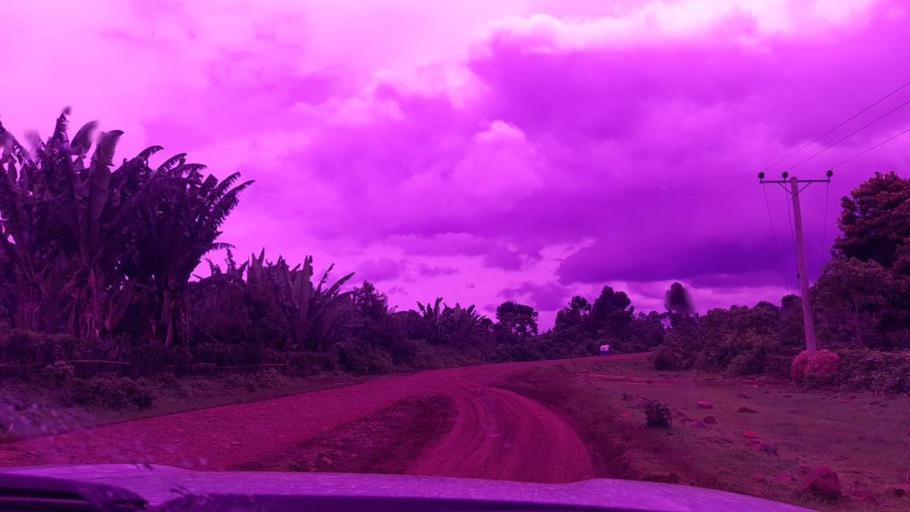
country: ET
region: Southern Nations, Nationalities, and People's Region
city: Tippi
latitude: 7.5747
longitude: 35.6360
